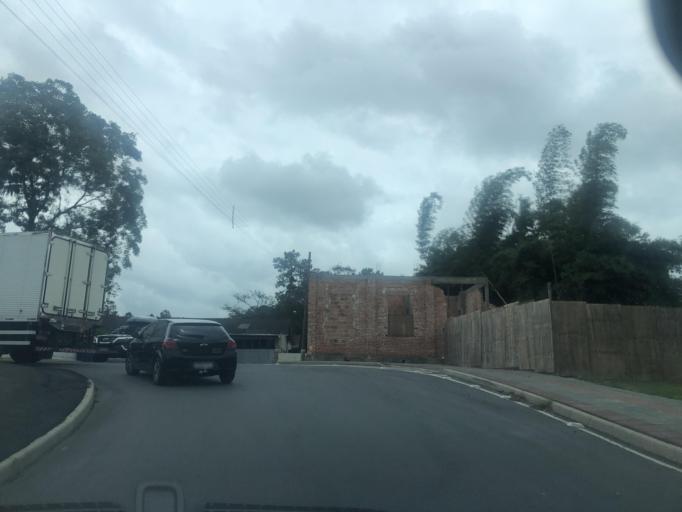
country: BR
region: Santa Catarina
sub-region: Joinville
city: Joinville
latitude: -26.3717
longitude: -48.7243
